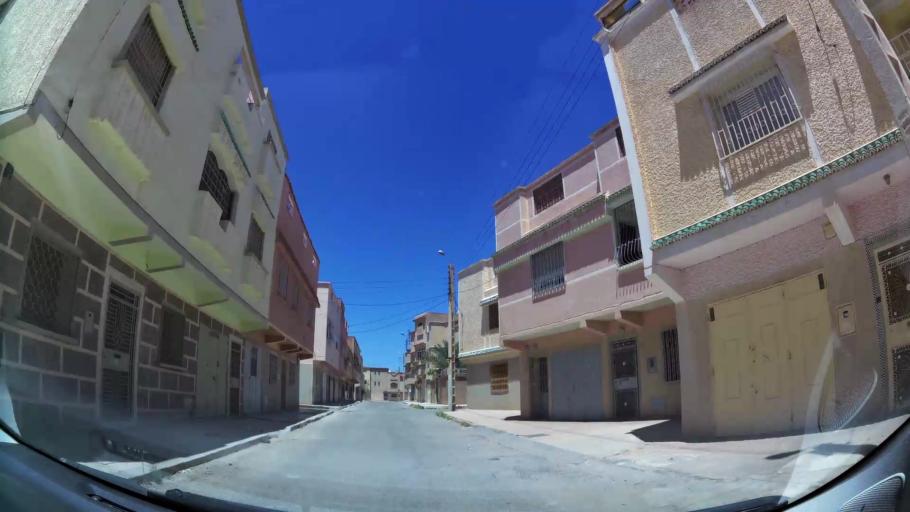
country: MA
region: Oriental
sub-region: Oujda-Angad
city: Oujda
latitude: 34.6765
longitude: -1.8779
